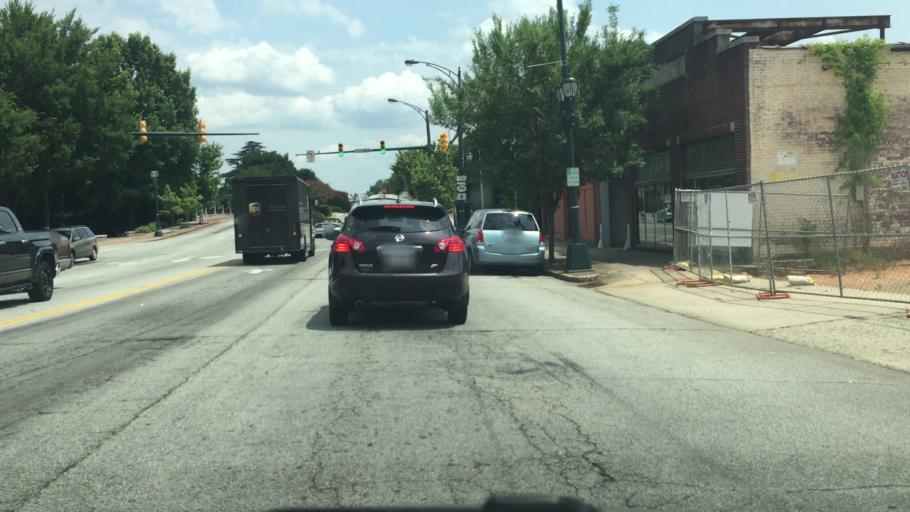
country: US
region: North Carolina
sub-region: Rowan County
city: Salisbury
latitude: 35.6663
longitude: -80.4687
